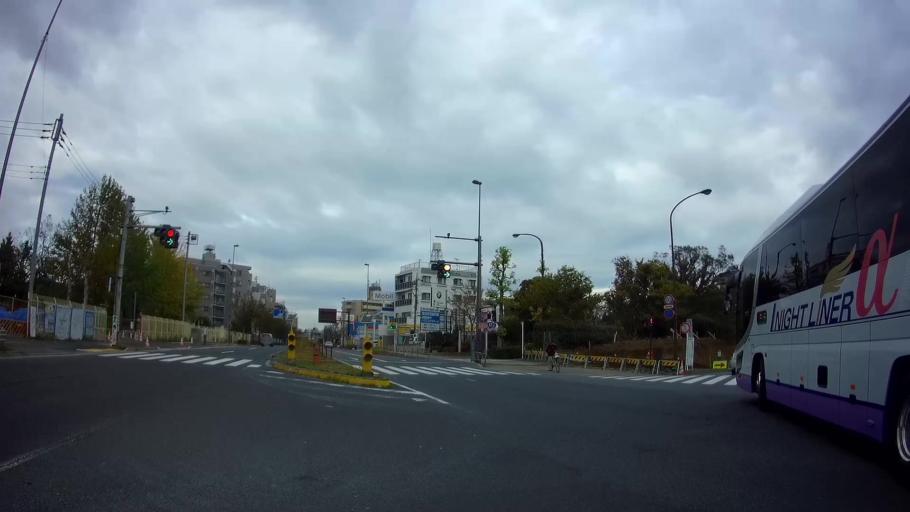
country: JP
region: Saitama
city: Wako
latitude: 35.7673
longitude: 139.6530
